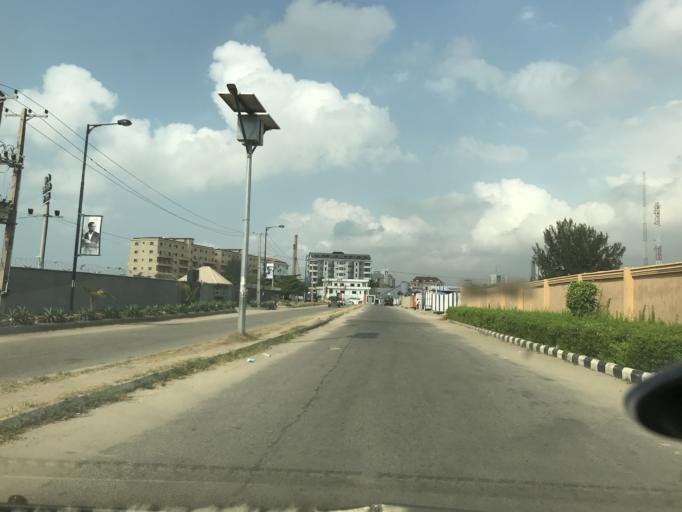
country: NG
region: Lagos
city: Ikoyi
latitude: 6.4242
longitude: 3.4432
